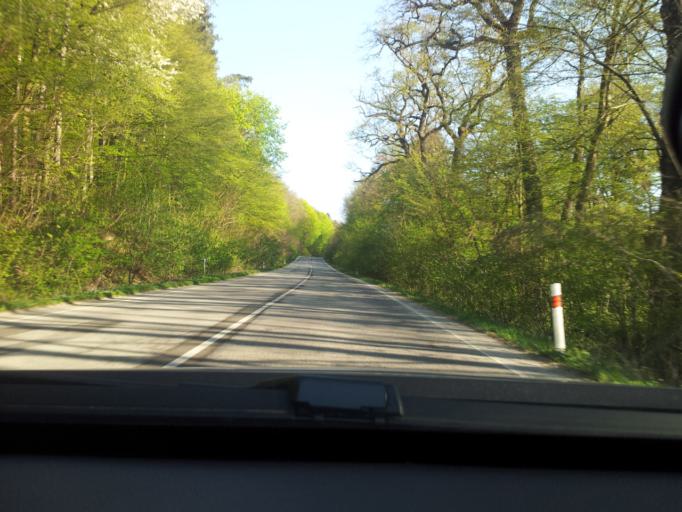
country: SK
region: Nitriansky
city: Zlate Moravce
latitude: 48.4361
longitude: 18.4113
